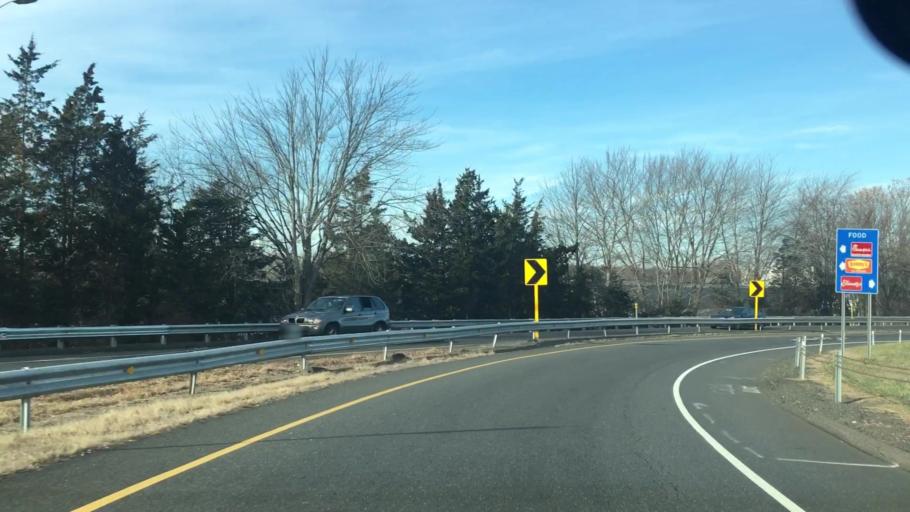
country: US
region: Connecticut
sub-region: Hartford County
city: Plainville
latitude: 41.6322
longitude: -72.8755
